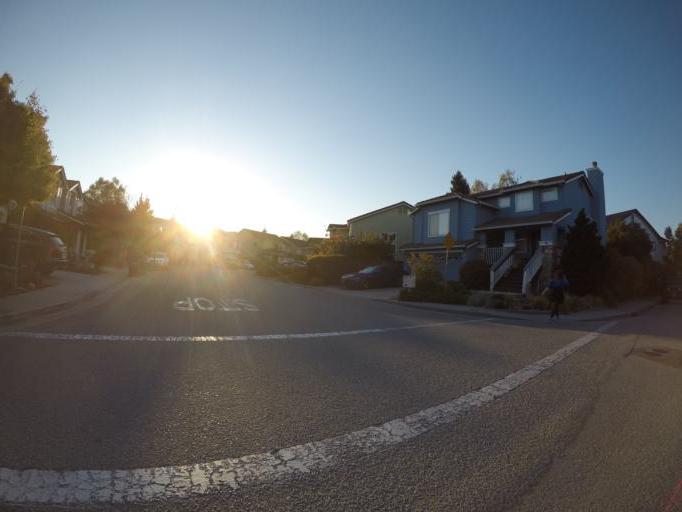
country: US
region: California
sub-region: Santa Cruz County
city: Scotts Valley
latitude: 37.0504
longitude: -122.0332
